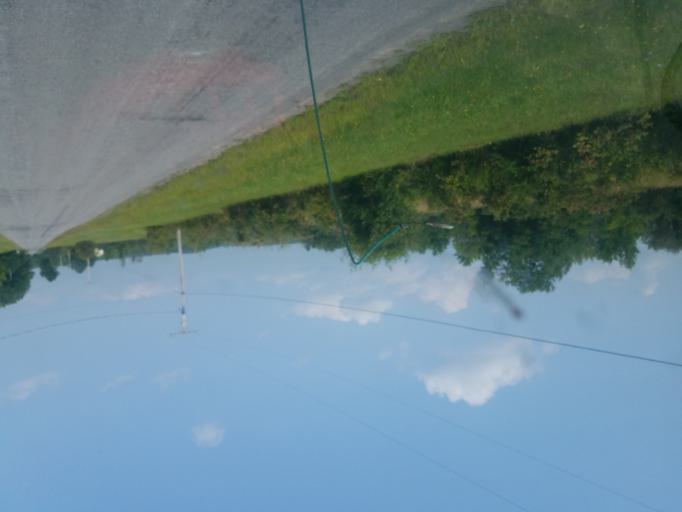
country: US
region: New York
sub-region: Montgomery County
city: Wellsville
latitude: 42.8518
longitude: -74.3432
